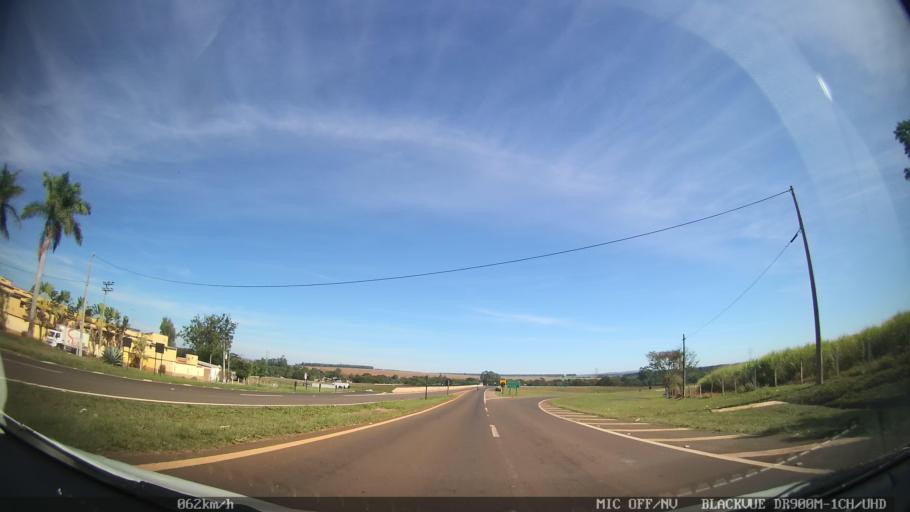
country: BR
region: Sao Paulo
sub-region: Porto Ferreira
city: Porto Ferreira
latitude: -21.8350
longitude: -47.4932
